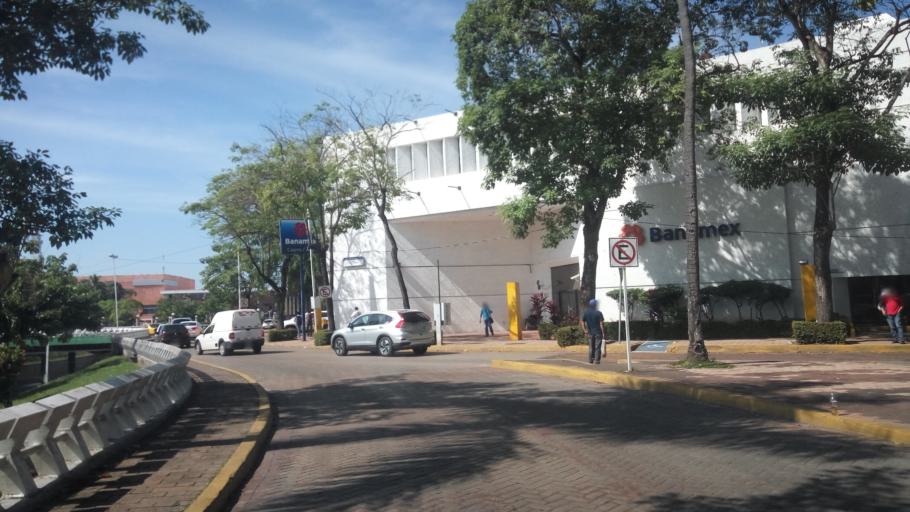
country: MX
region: Tabasco
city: Villahermosa
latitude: 17.9990
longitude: -92.9429
